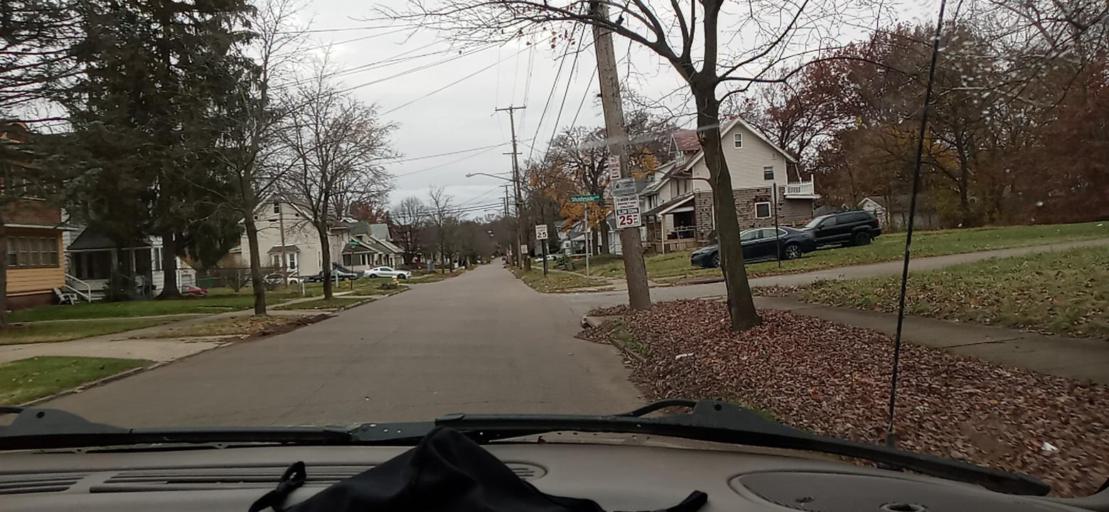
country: US
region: Ohio
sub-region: Summit County
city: Akron
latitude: 41.0876
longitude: -81.5476
